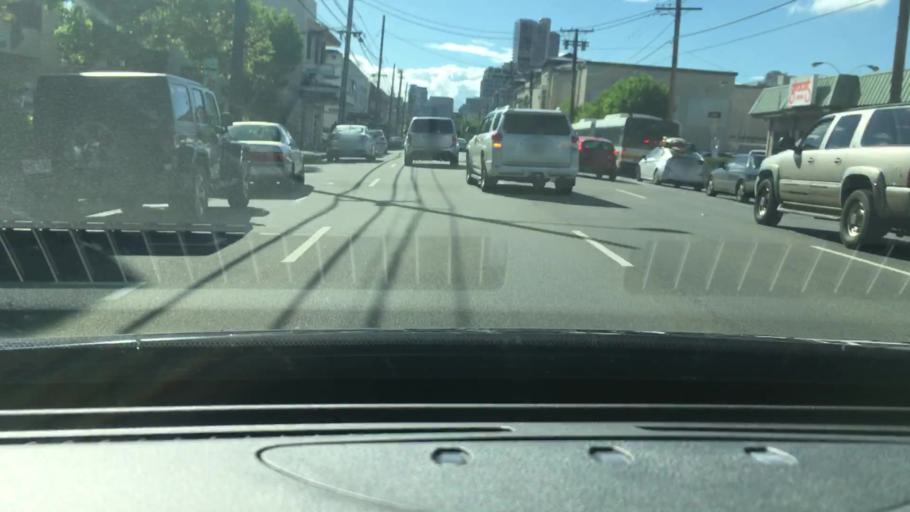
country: US
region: Hawaii
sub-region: Honolulu County
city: Honolulu
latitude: 21.3007
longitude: -157.8408
